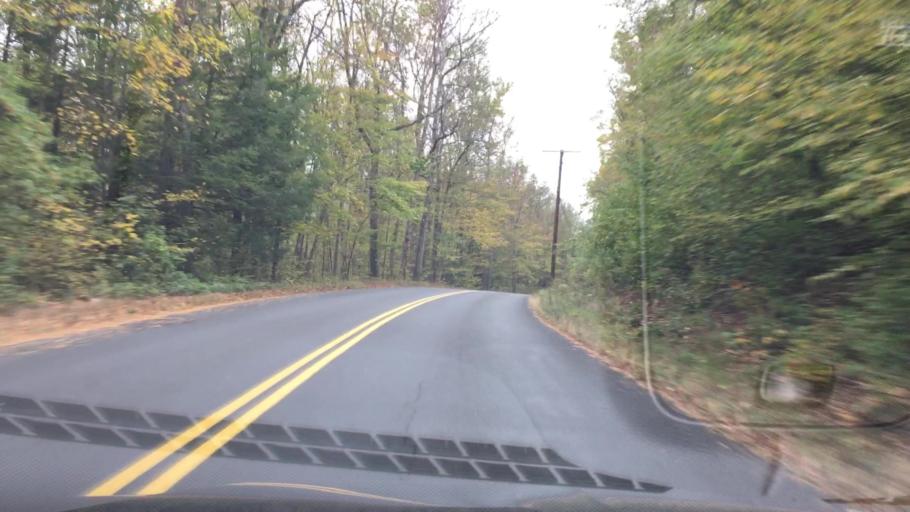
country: US
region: Connecticut
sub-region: Tolland County
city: Somers
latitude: 41.9657
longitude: -72.4115
